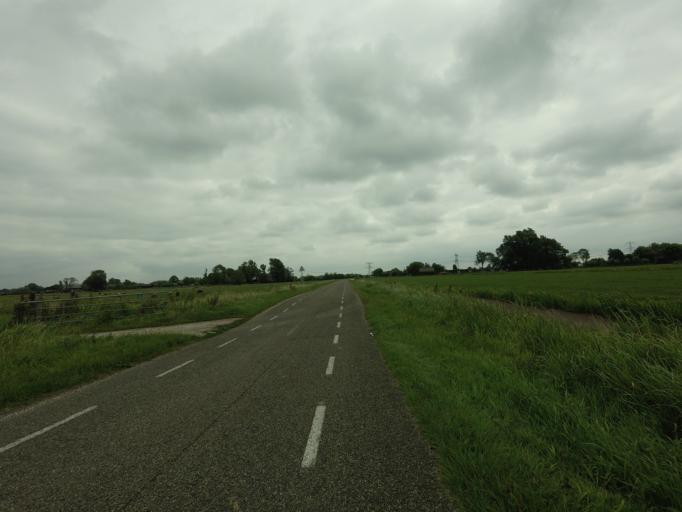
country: NL
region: Utrecht
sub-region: Stichtse Vecht
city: Breukelen
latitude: 52.2102
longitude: 4.9752
